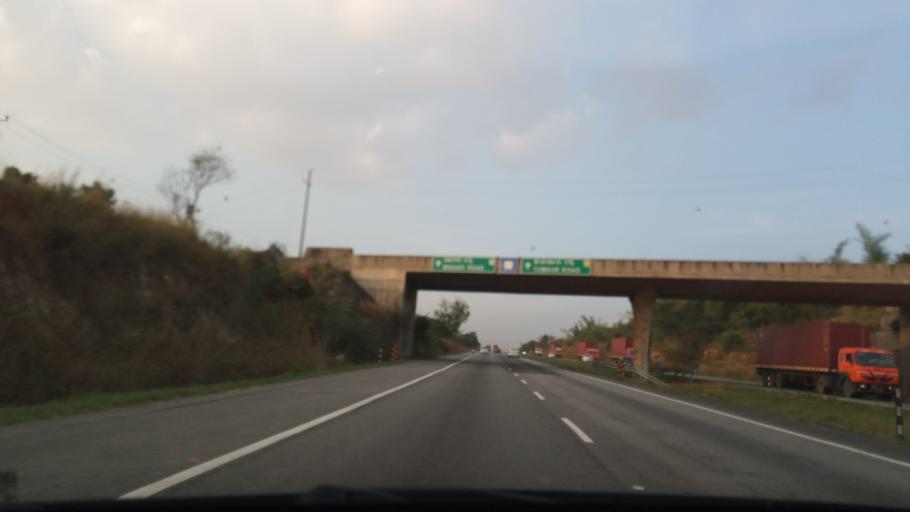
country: IN
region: Karnataka
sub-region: Bangalore Urban
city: Bangalore
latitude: 12.9617
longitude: 77.4713
